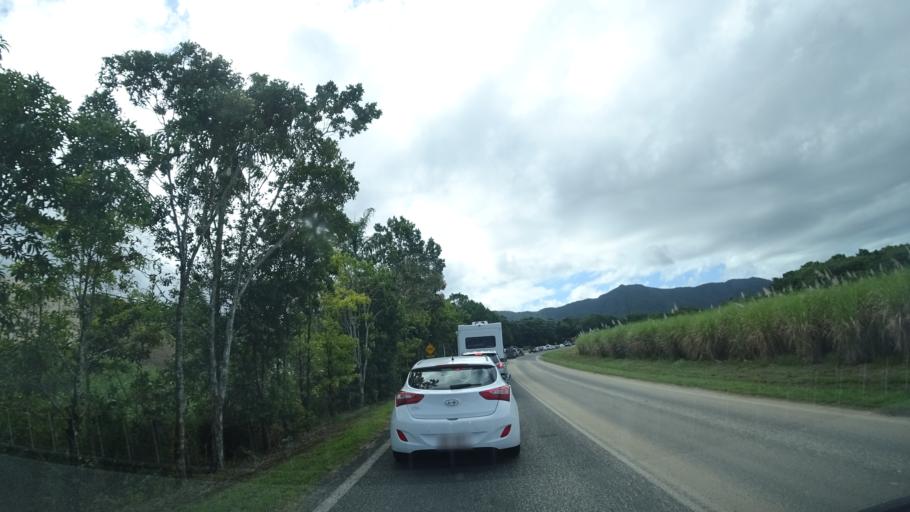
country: AU
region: Queensland
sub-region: Cairns
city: Port Douglas
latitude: -16.2630
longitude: 145.3929
